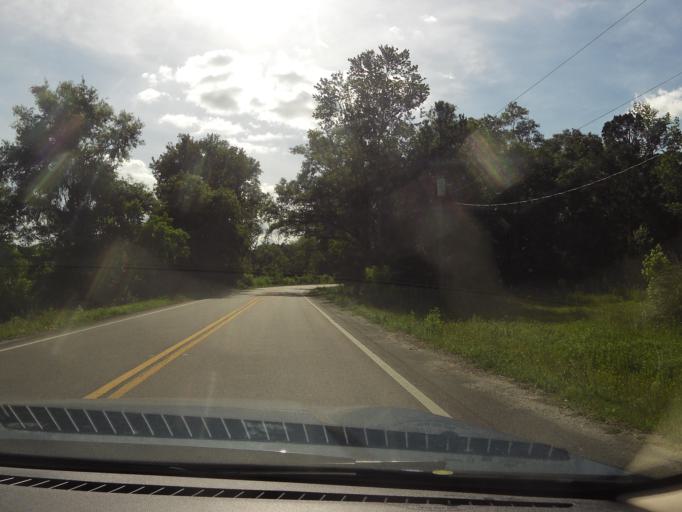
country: US
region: Florida
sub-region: Nassau County
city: Callahan
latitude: 30.5610
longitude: -81.8393
